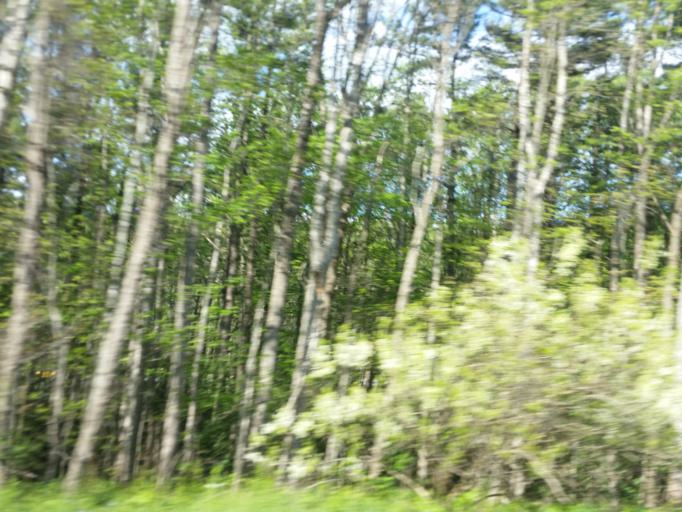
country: US
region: West Virginia
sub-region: Raleigh County
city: Shady Spring
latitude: 37.6740
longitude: -81.1169
